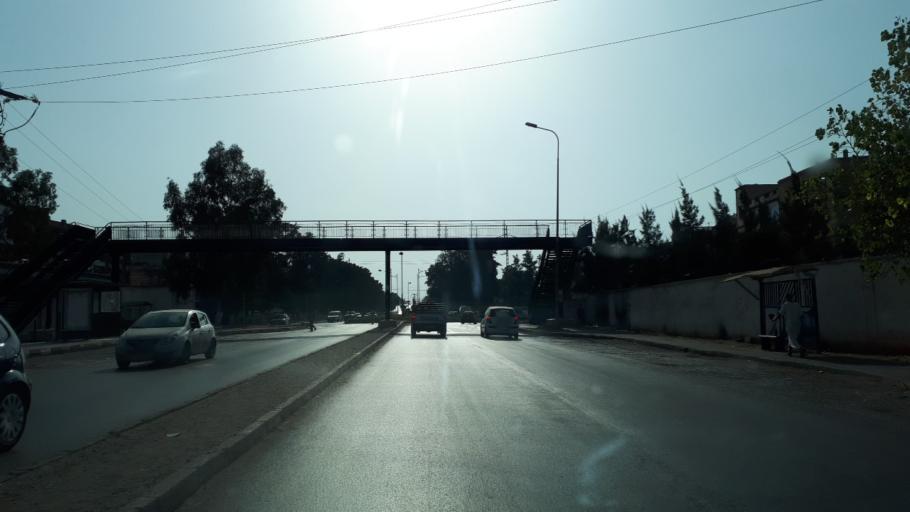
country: DZ
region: Alger
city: Dar el Beida
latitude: 36.7283
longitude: 3.2180
